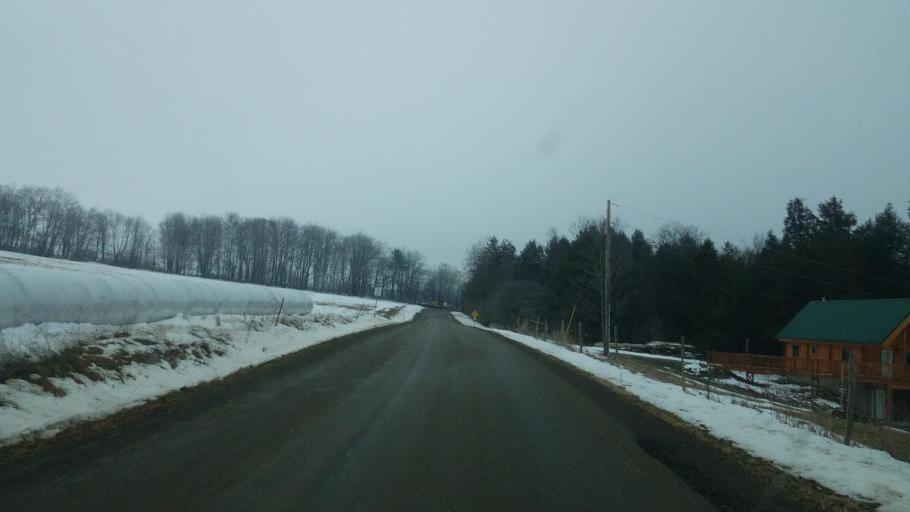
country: US
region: New York
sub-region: Allegany County
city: Andover
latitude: 41.9950
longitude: -77.7656
